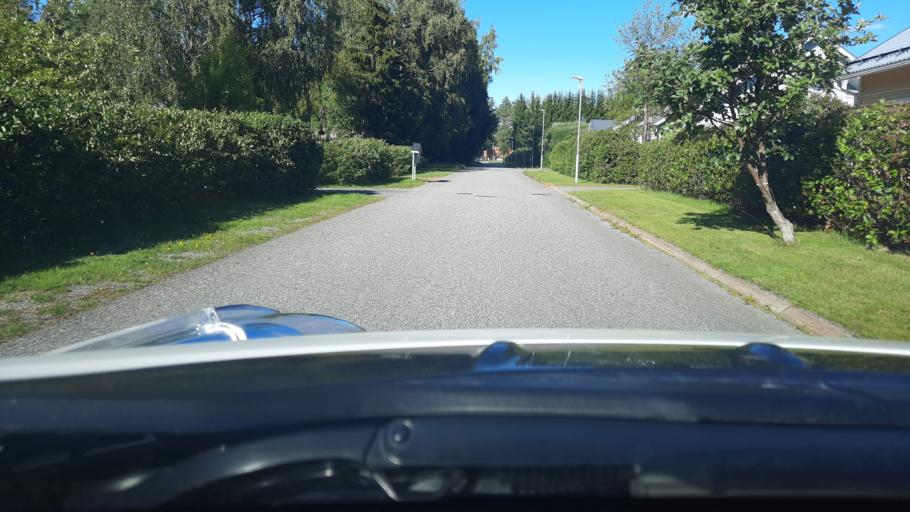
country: FI
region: North Karelia
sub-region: Joensuu
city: Joensuu
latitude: 62.6359
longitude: 29.6846
